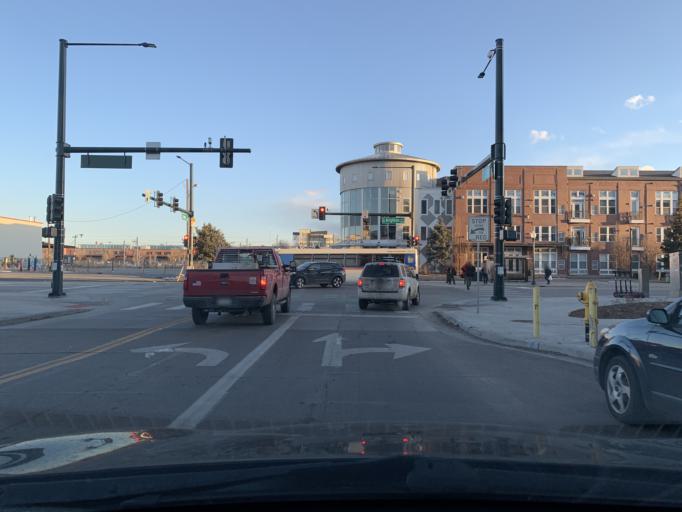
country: US
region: Colorado
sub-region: Denver County
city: Denver
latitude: 39.7646
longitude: -104.9868
